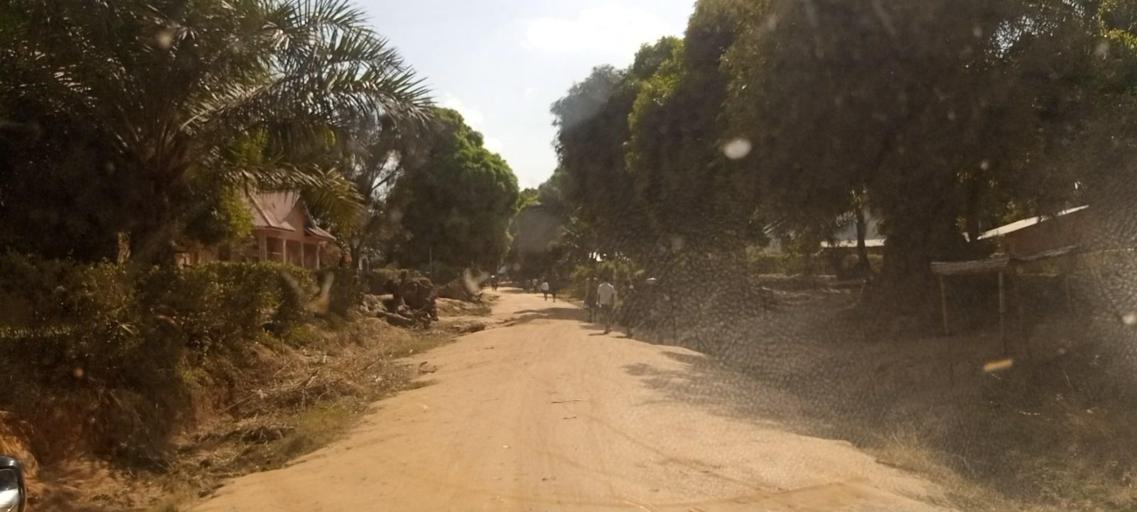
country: CD
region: Kasai-Oriental
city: Kabinda
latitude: -6.1286
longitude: 24.5024
